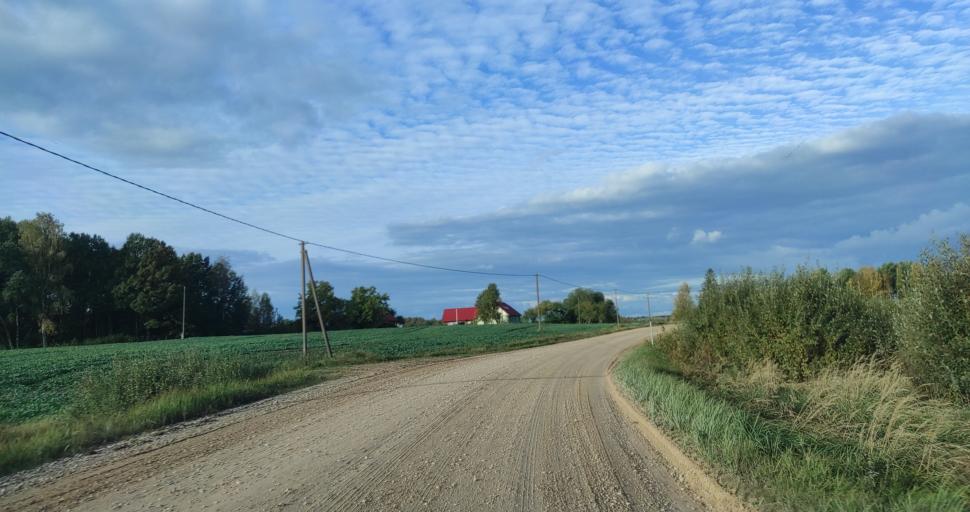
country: LV
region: Skrunda
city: Skrunda
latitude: 56.7466
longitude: 21.8134
